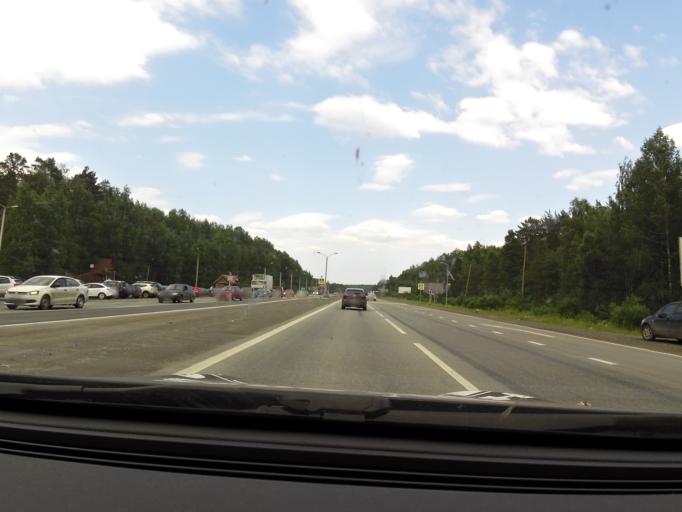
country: RU
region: Sverdlovsk
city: Severka
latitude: 56.8420
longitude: 60.1975
